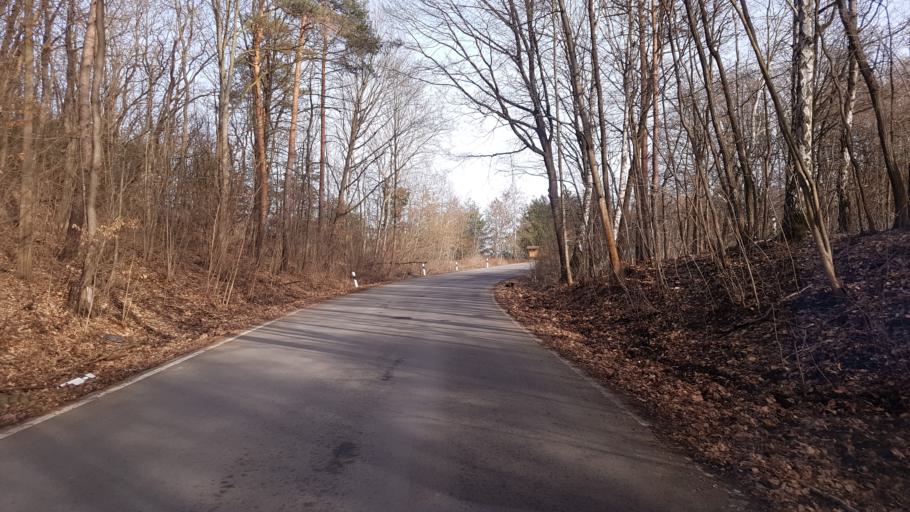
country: DE
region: Brandenburg
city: Schipkau
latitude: 51.5294
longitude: 13.8264
